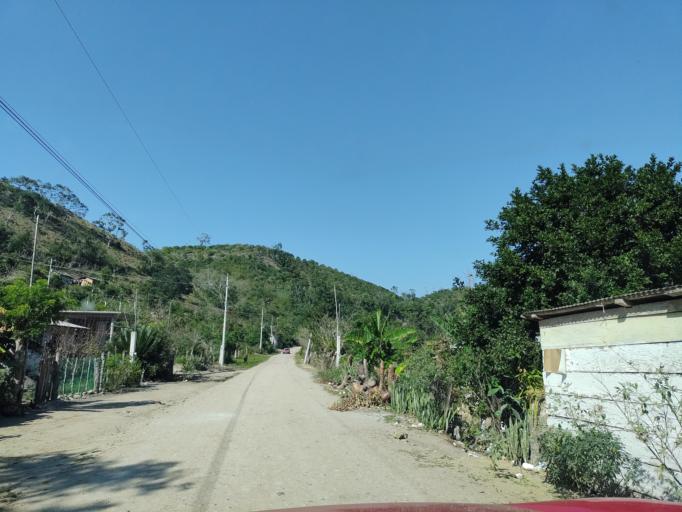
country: MX
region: Veracruz
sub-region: Papantla
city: Polutla
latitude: 20.4969
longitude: -97.1786
